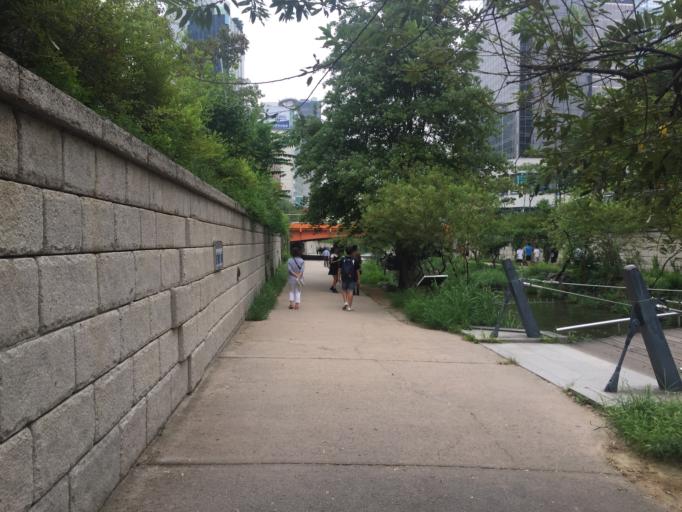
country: KR
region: Seoul
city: Seoul
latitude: 37.5689
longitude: 126.9818
